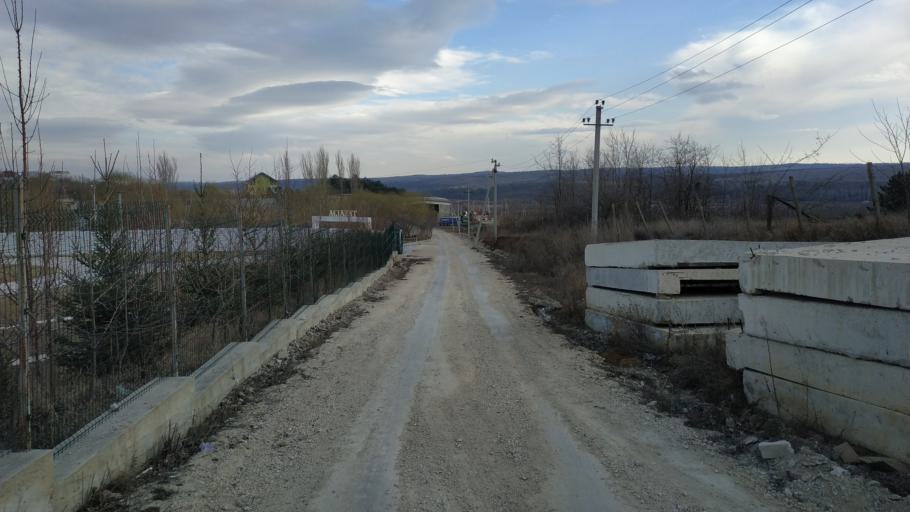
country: MD
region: Laloveni
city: Ialoveni
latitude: 46.9610
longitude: 28.7475
